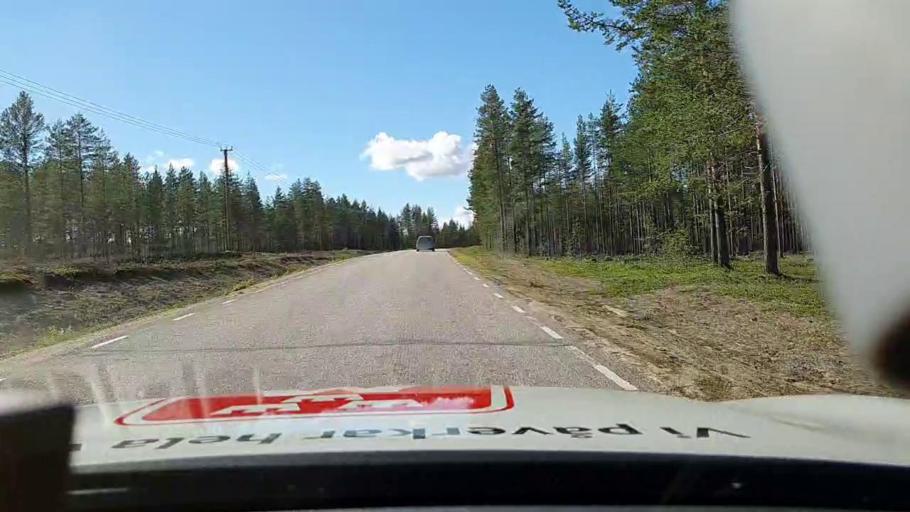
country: SE
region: Norrbotten
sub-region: Overkalix Kommun
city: OEverkalix
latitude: 66.2499
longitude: 22.8831
